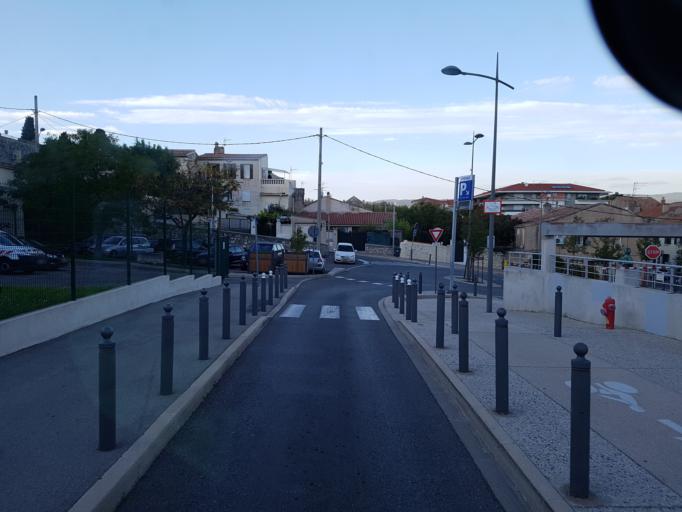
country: FR
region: Provence-Alpes-Cote d'Azur
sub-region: Departement des Bouches-du-Rhone
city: La Ciotat
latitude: 43.1729
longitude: 5.6029
